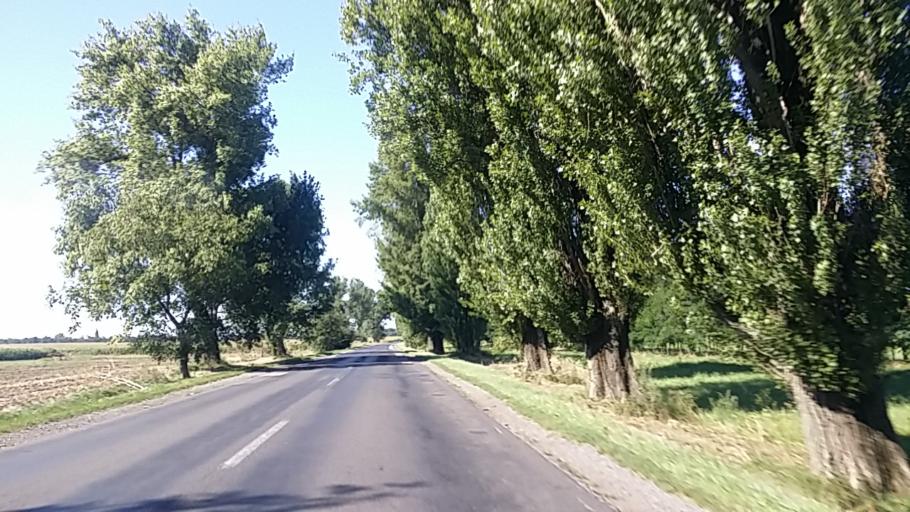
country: HU
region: Fejer
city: Mezofalva
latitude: 46.9355
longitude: 18.7990
